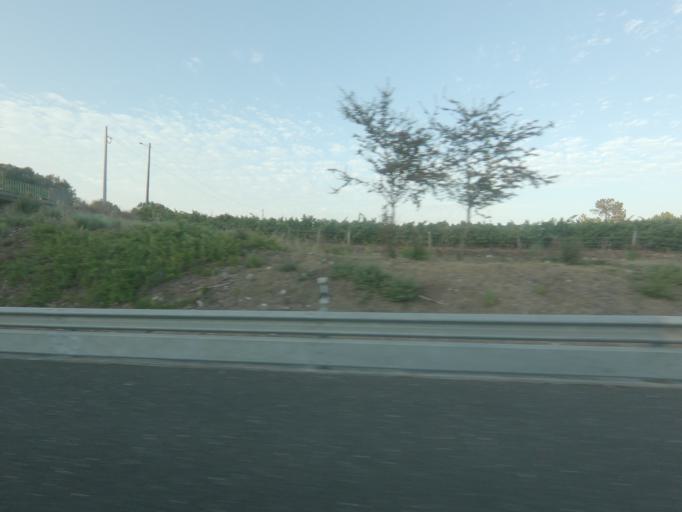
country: PT
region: Leiria
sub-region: Leiria
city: Santa Catarina da Serra
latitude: 39.6945
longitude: -8.6935
